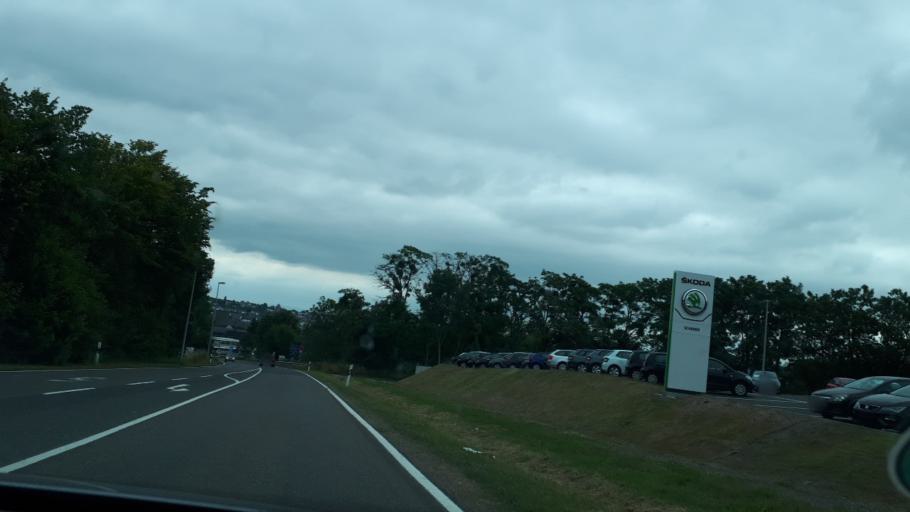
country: DE
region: Rheinland-Pfalz
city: Mayen
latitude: 50.3238
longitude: 7.2088
